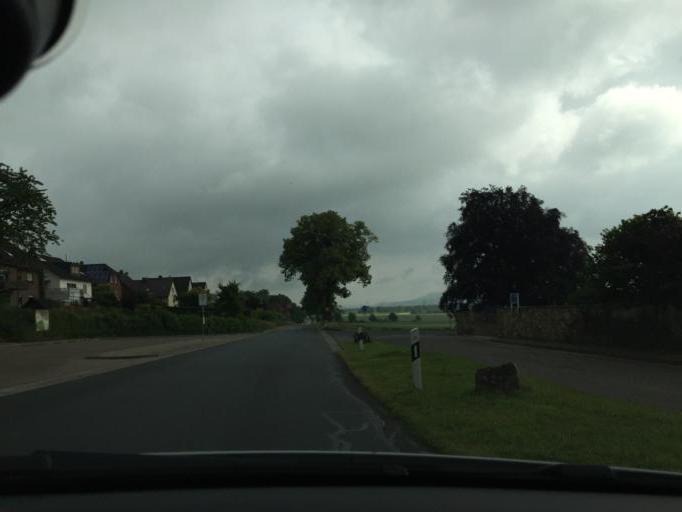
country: DE
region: Lower Saxony
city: Hameln
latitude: 52.0289
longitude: 9.3444
